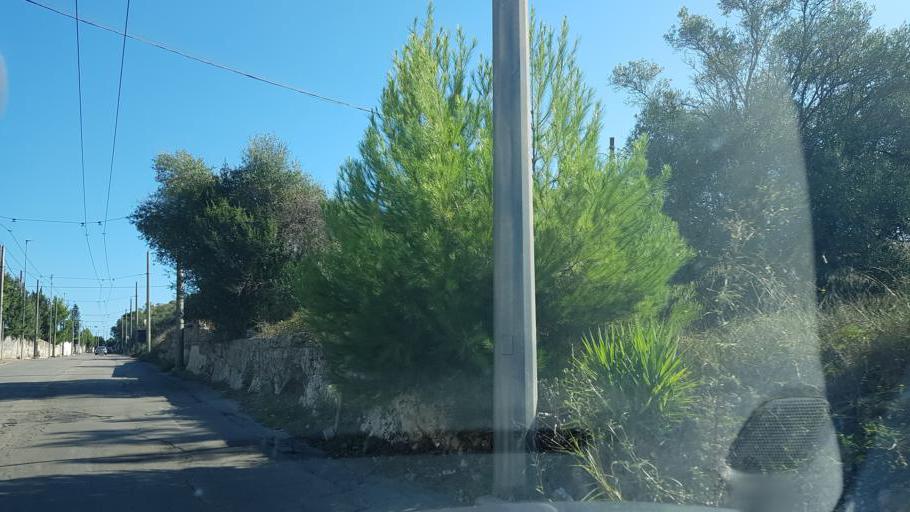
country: IT
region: Apulia
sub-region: Provincia di Lecce
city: Lequile
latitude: 40.3413
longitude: 18.1383
